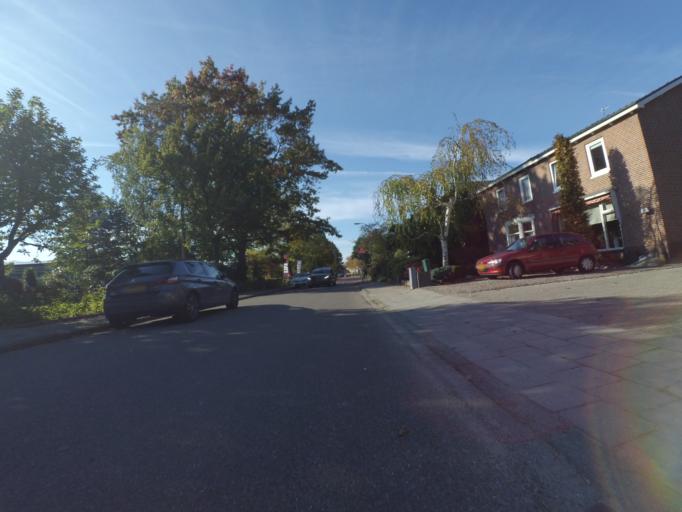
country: NL
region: Gelderland
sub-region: Gemeente Nijkerk
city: Nijkerk
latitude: 52.2216
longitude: 5.5000
